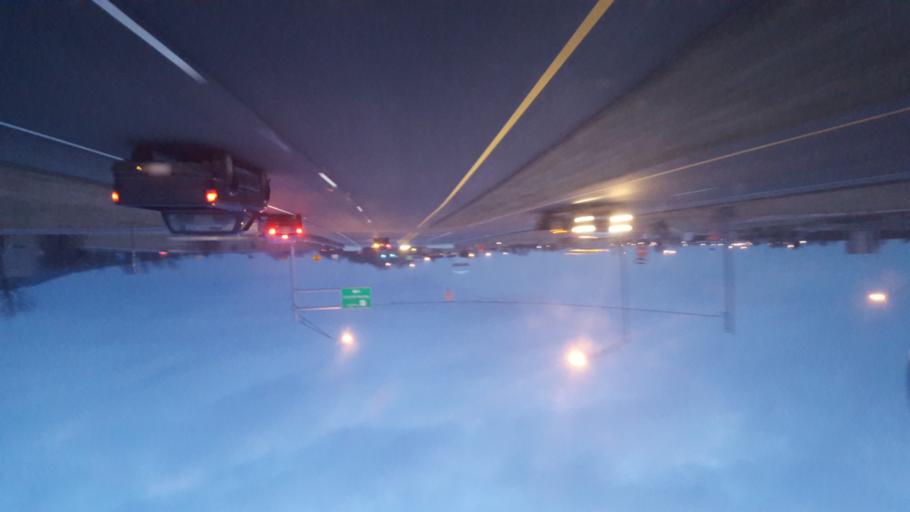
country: US
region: Ohio
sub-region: Ross County
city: Chillicothe
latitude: 39.3862
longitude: -82.9712
